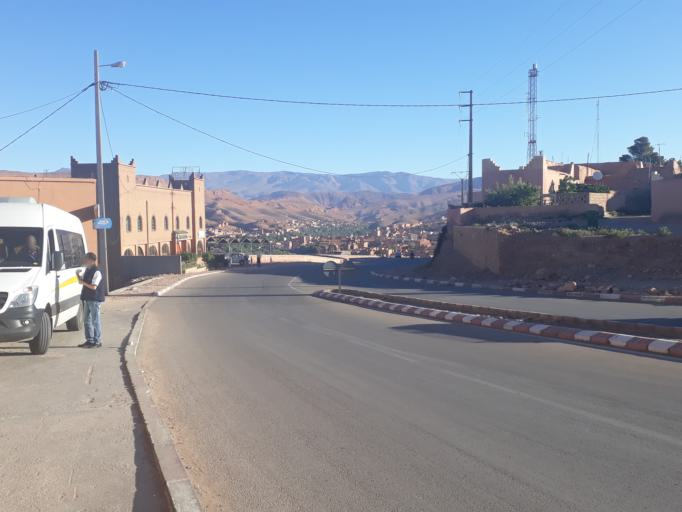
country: MA
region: Souss-Massa-Draa
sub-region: Ouarzazate
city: Imider
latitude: 31.3666
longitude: -5.9867
